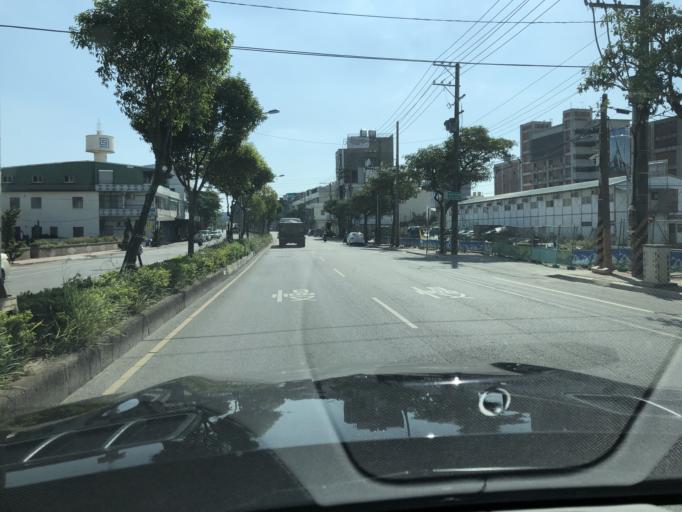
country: TW
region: Taiwan
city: Taoyuan City
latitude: 25.0794
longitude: 121.2857
